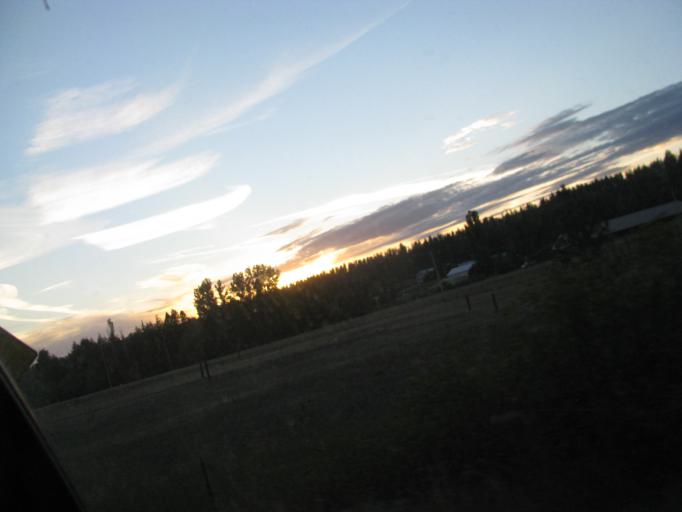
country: US
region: Washington
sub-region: Spokane County
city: Mead
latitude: 47.8899
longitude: -117.3508
